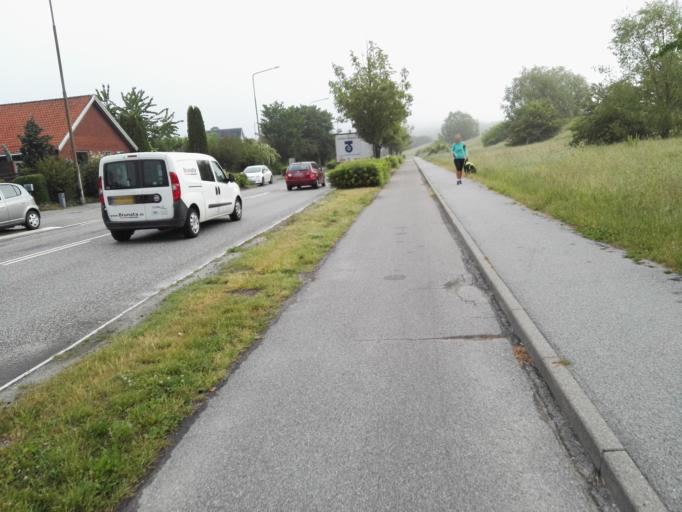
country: DK
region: Capital Region
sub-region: Ballerup Kommune
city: Ballerup
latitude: 55.7487
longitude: 12.3710
